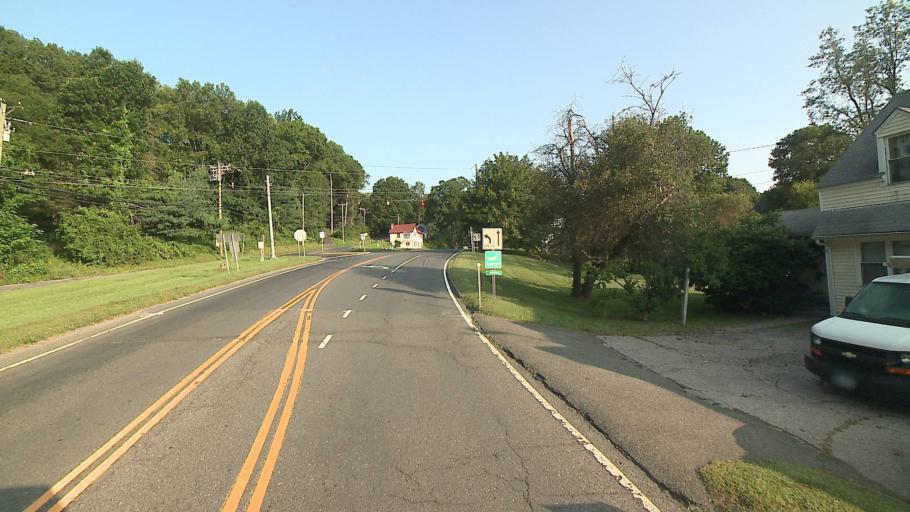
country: US
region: Connecticut
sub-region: Fairfield County
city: Sherman
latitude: 41.5946
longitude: -73.4566
